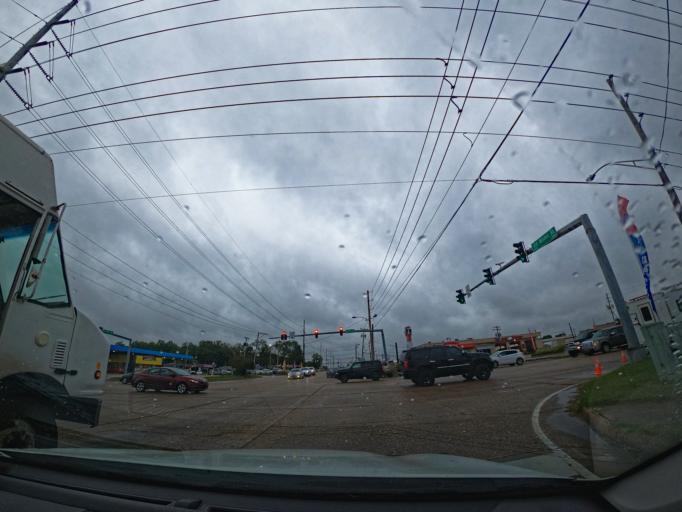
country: US
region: Louisiana
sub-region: Bossier Parish
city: Bossier City
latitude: 32.5212
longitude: -93.6967
